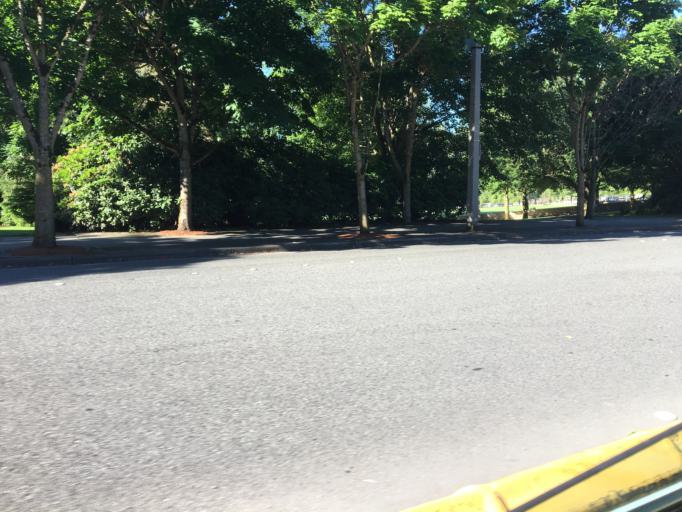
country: US
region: Washington
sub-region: King County
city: Bellevue
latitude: 47.6139
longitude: -122.2027
